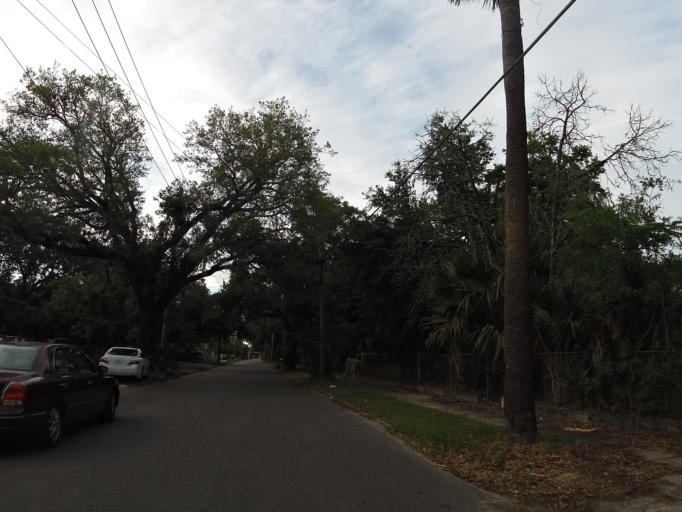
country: US
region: Florida
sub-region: Duval County
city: Jacksonville
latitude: 30.3500
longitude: -81.6433
